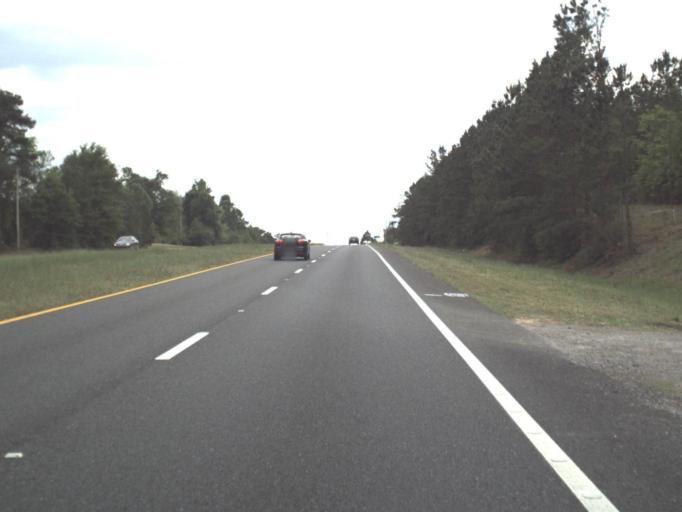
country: US
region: Florida
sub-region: Escambia County
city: Century
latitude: 30.8807
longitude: -87.3218
